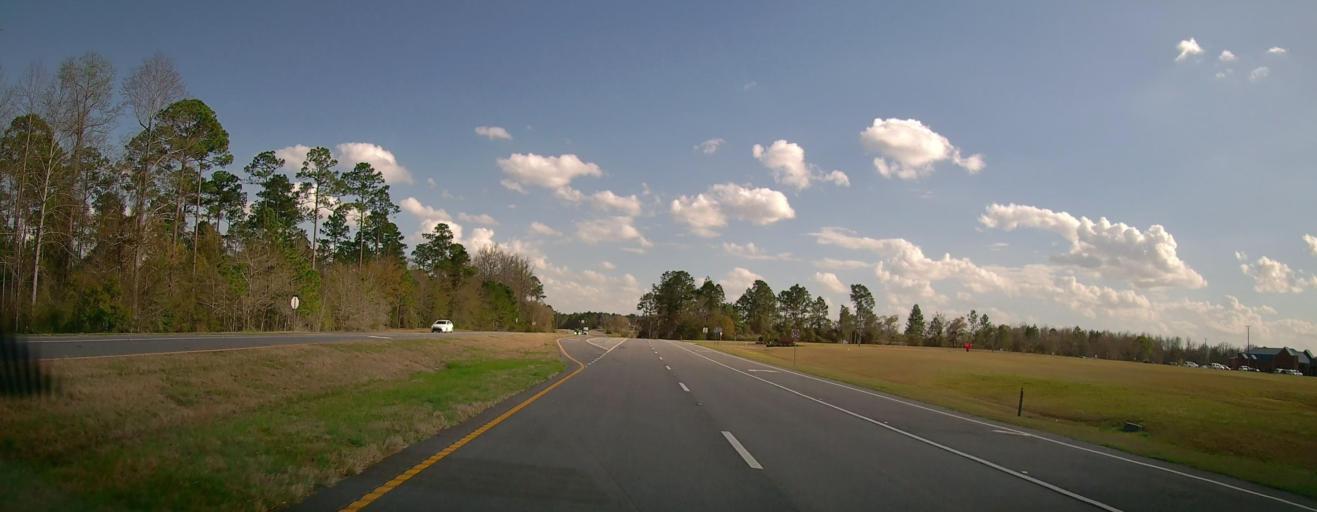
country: US
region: Georgia
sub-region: Telfair County
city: McRae
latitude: 32.0508
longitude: -82.8611
